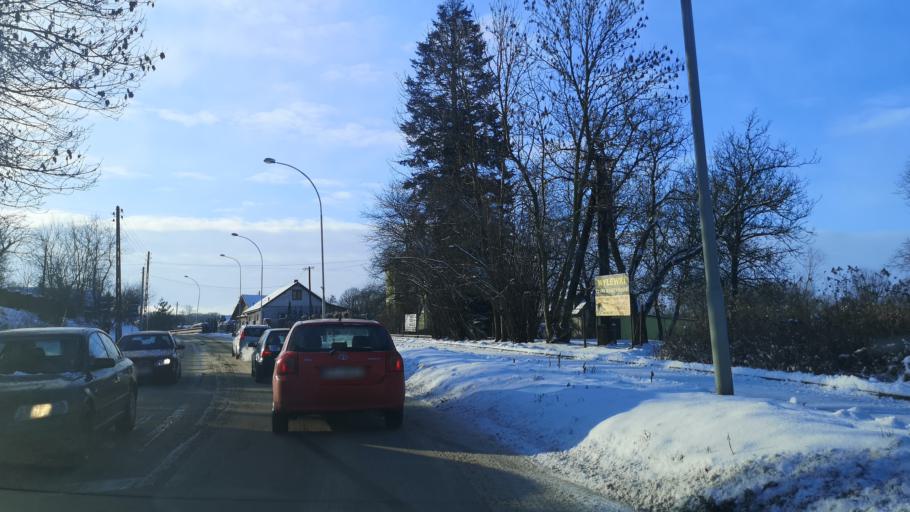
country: PL
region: Subcarpathian Voivodeship
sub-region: Powiat przeworski
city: Przeworsk
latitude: 50.0714
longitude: 22.4904
